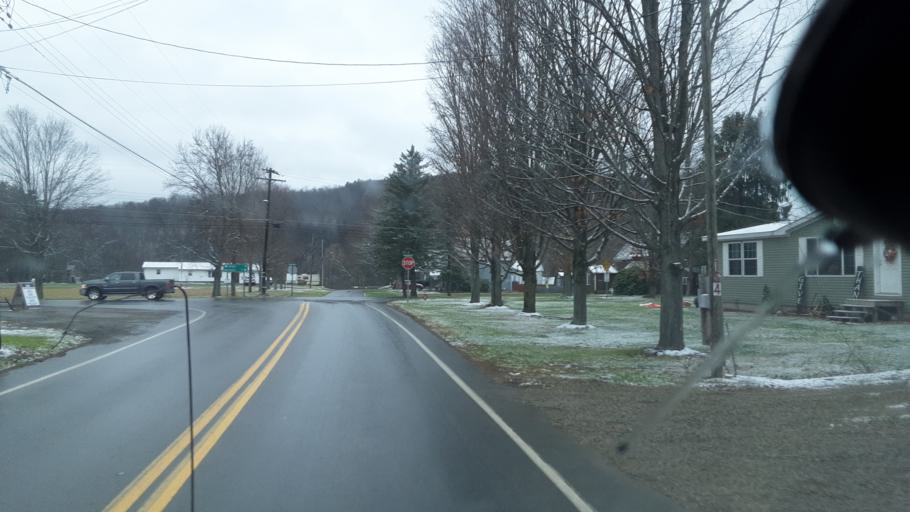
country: US
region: Pennsylvania
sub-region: Potter County
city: Shinglehouse
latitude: 41.9662
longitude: -78.1869
